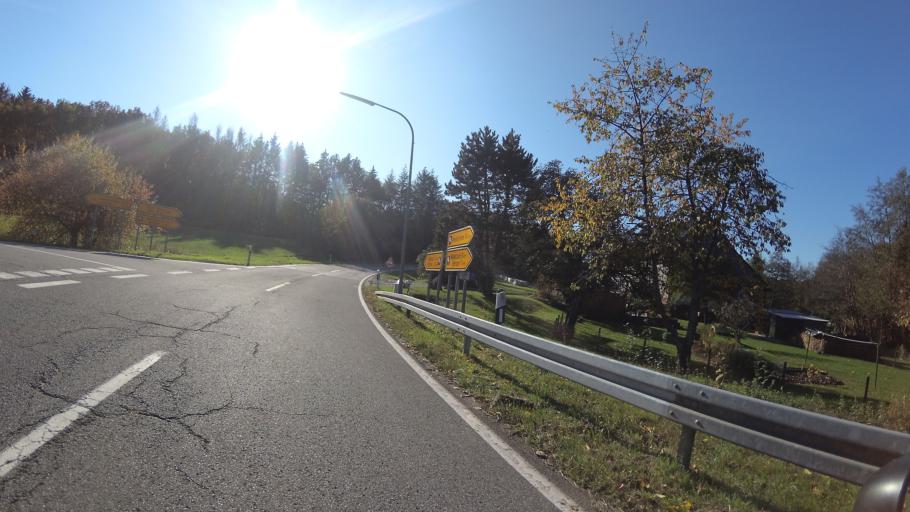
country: DE
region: Saarland
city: Britten
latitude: 49.5261
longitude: 6.7017
